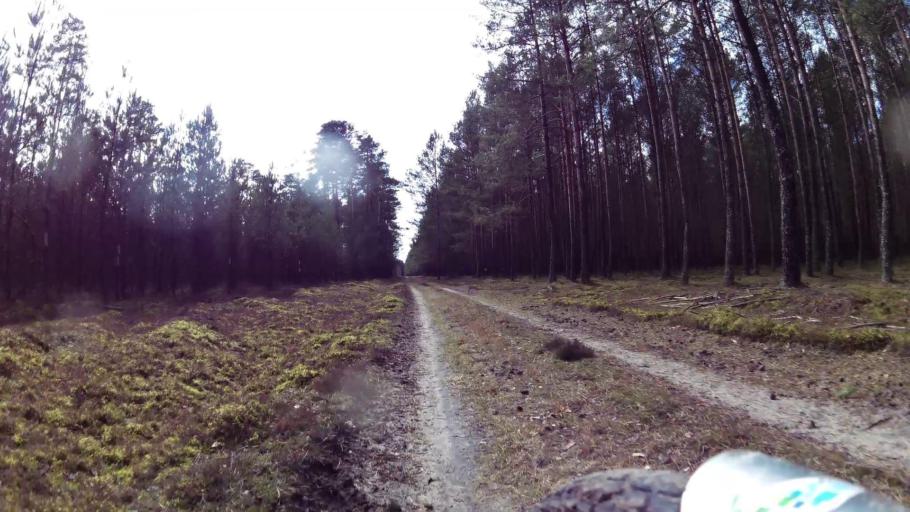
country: PL
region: Pomeranian Voivodeship
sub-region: Powiat bytowski
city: Kolczyglowy
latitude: 54.1919
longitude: 17.2150
